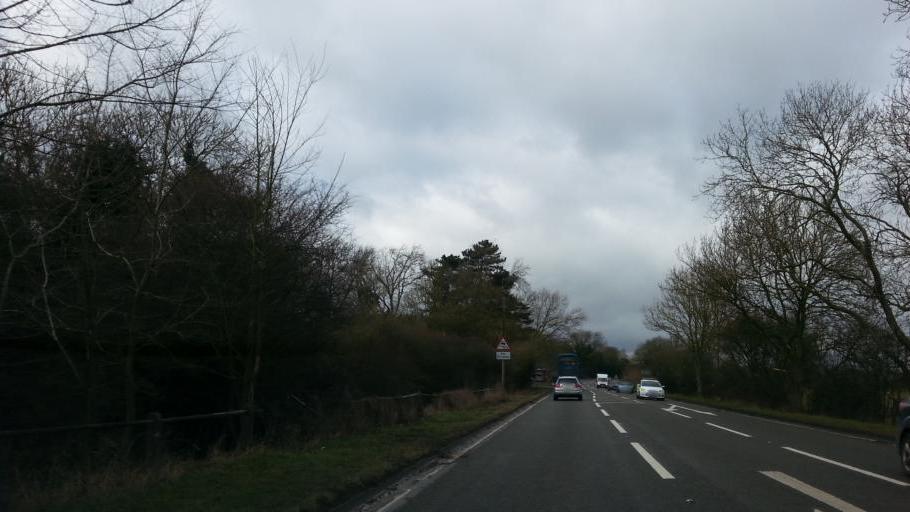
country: GB
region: England
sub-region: Leicestershire
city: Kibworth Harcourt
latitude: 52.5226
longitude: -0.9616
